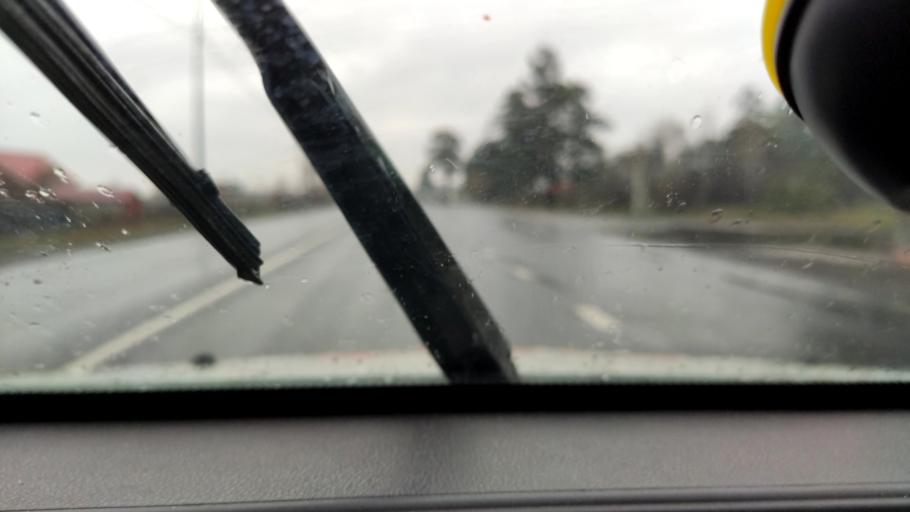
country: RU
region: Samara
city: Povolzhskiy
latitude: 53.5843
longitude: 49.5701
